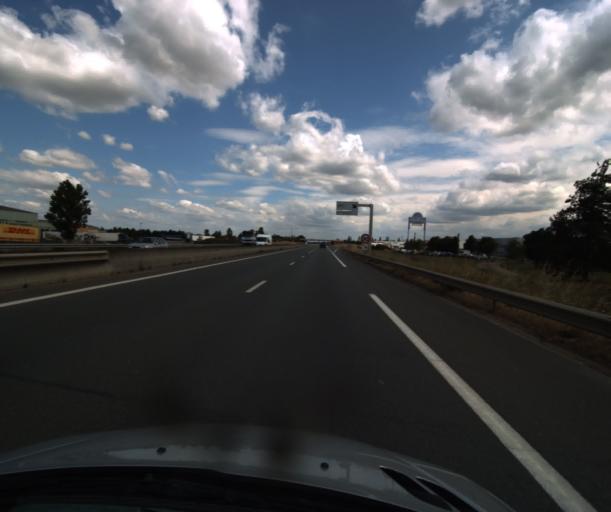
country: FR
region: Midi-Pyrenees
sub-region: Departement du Tarn-et-Garonne
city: Bressols
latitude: 43.9357
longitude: 1.3208
